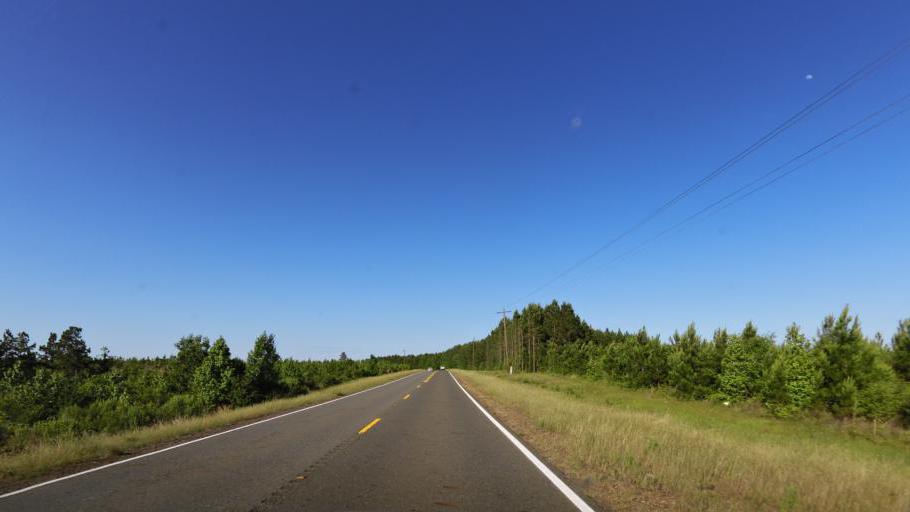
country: US
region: Louisiana
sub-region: Sabine Parish
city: Many
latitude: 31.4147
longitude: -93.5860
